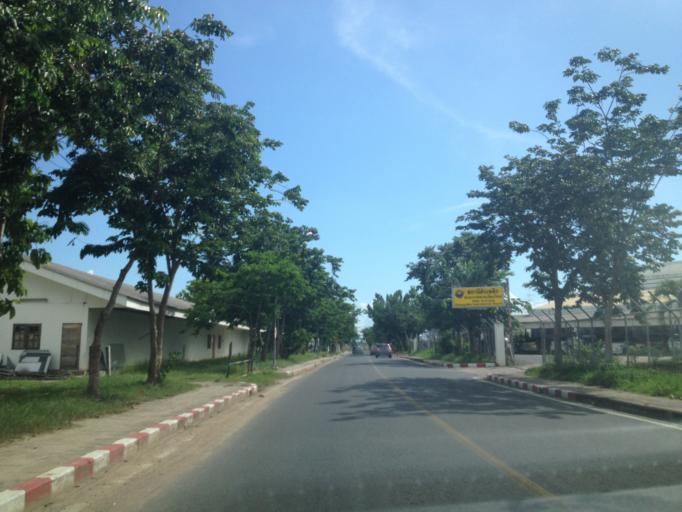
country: TH
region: Chiang Mai
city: Chiang Mai
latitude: 18.7629
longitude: 98.9686
